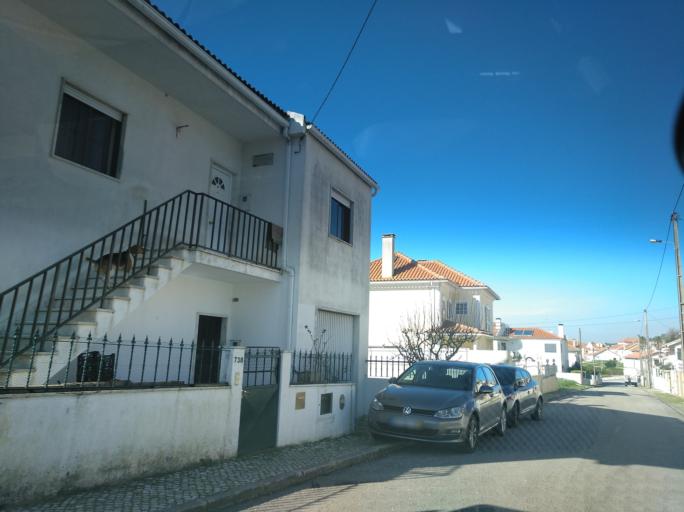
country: PT
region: Lisbon
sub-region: Odivelas
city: Canecas
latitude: 38.8050
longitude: -9.2181
